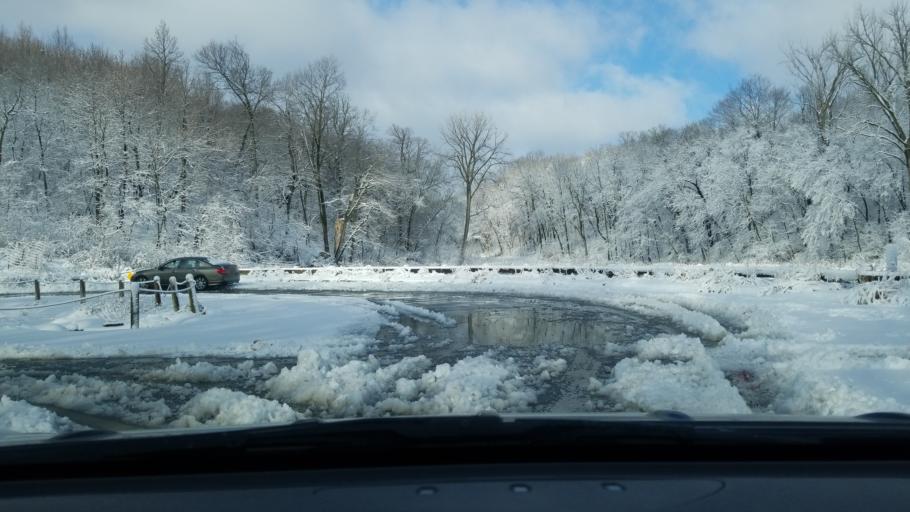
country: US
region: Nebraska
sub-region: Douglas County
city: Omaha
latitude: 41.2212
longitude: -95.9419
